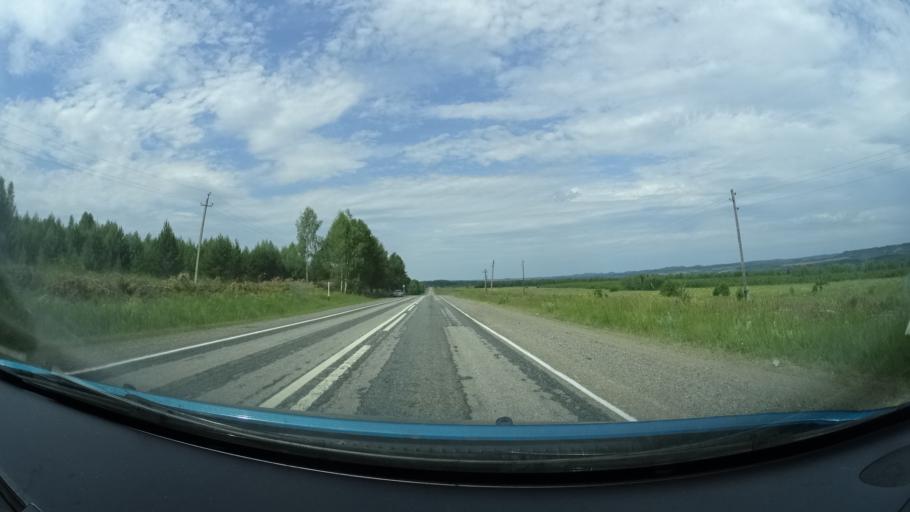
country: RU
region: Perm
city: Osa
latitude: 57.1280
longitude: 55.5251
